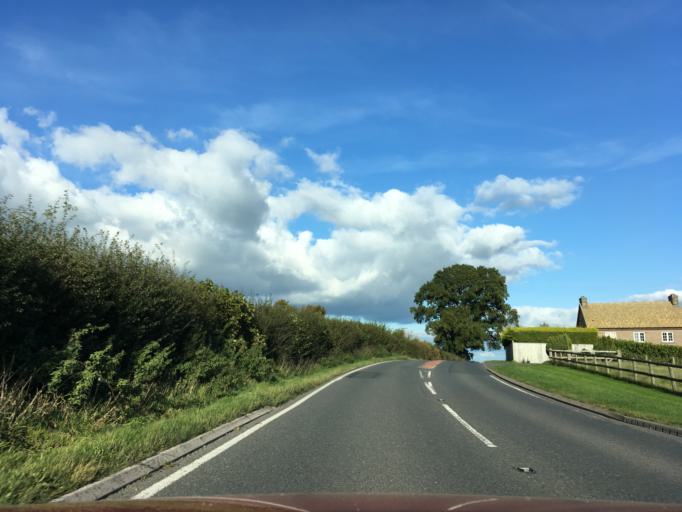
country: GB
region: Wales
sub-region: Sir Powys
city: Hay
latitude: 52.0111
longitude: -3.2423
